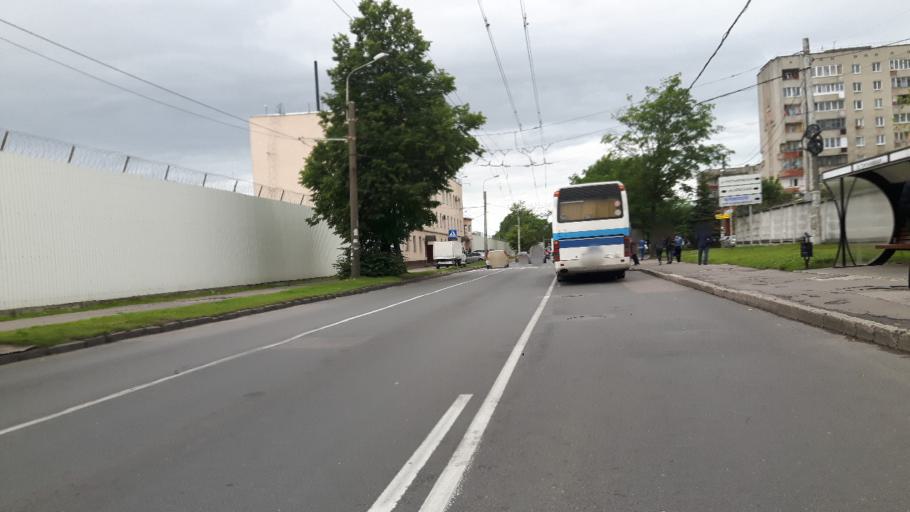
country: RU
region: Kaliningrad
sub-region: Gorod Kaliningrad
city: Kaliningrad
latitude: 54.7395
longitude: 20.4775
